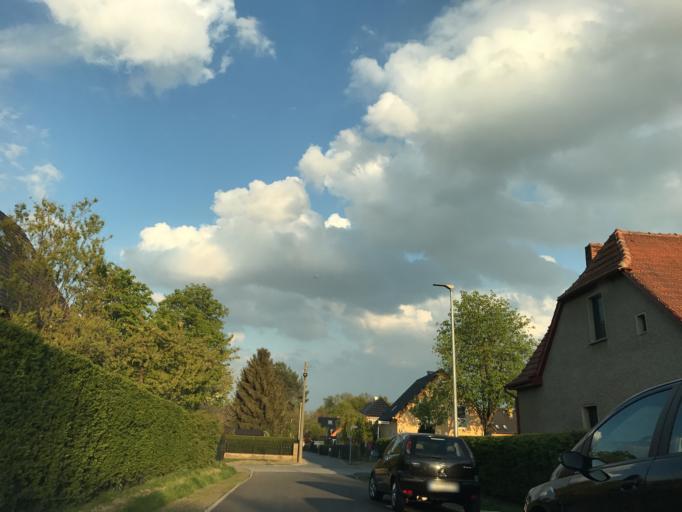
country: DE
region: Brandenburg
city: Falkensee
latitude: 52.5500
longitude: 13.0815
